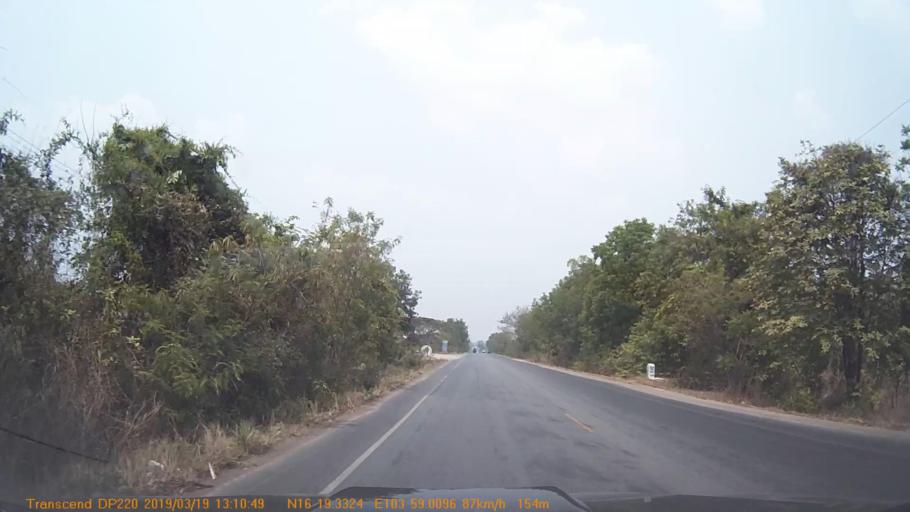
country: TH
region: Roi Et
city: Waeng
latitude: 16.3226
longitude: 103.9836
